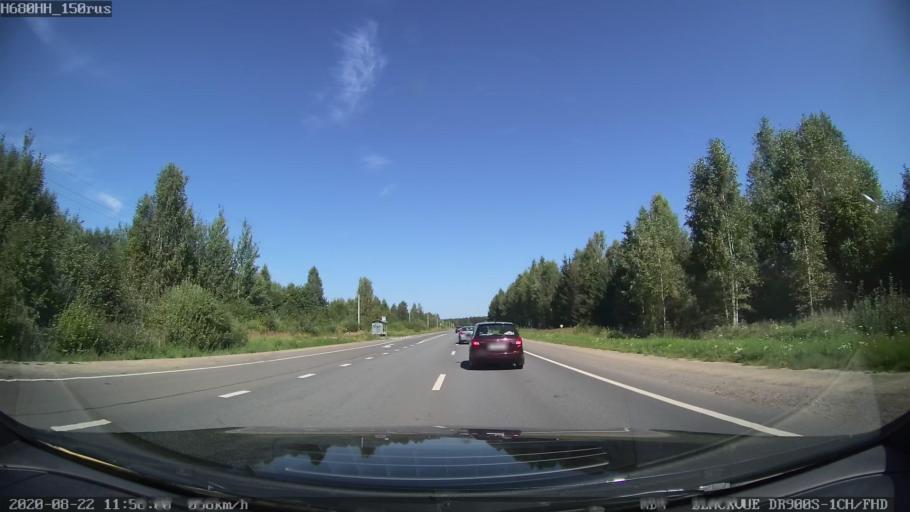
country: RU
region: Tverskaya
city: Rameshki
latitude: 57.1861
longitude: 36.0825
